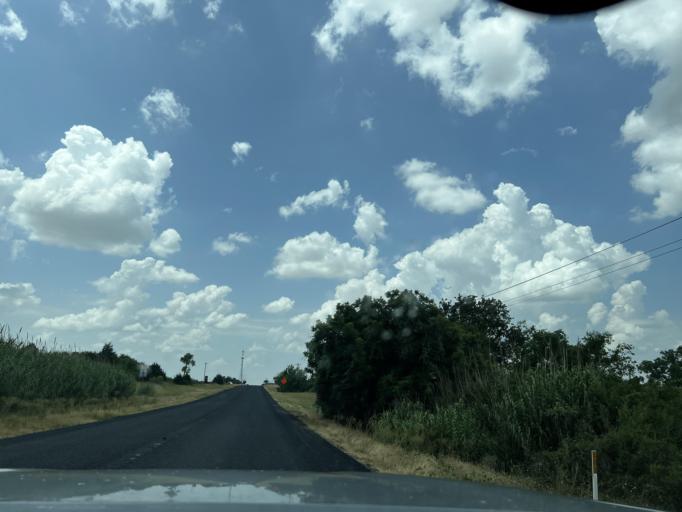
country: US
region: Texas
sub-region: Wise County
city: Boyd
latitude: 33.0739
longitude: -97.6499
